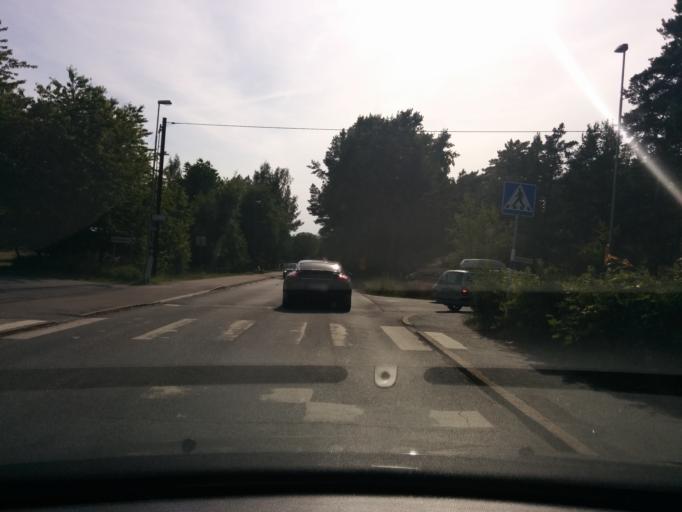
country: SE
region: Stockholm
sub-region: Varmdo Kommun
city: Holo
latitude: 59.3108
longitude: 18.6966
